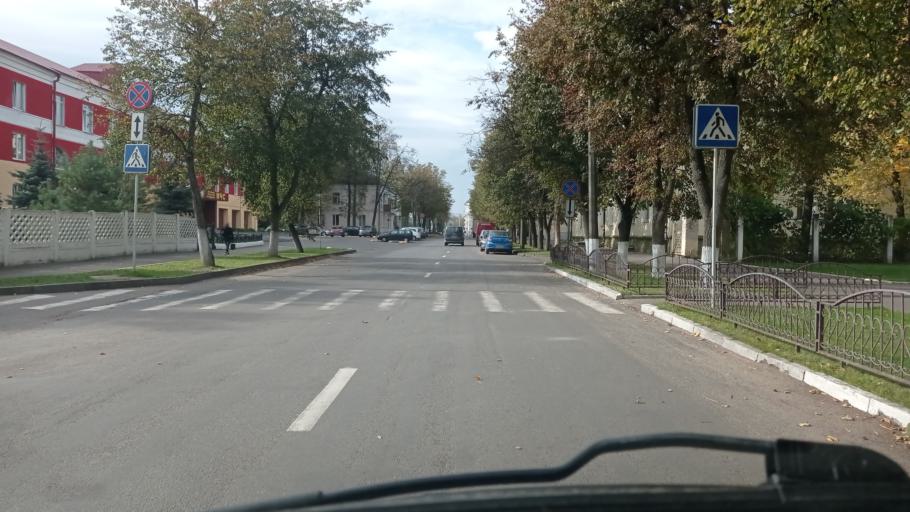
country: BY
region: Vitebsk
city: Vitebsk
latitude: 55.1837
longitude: 30.2101
